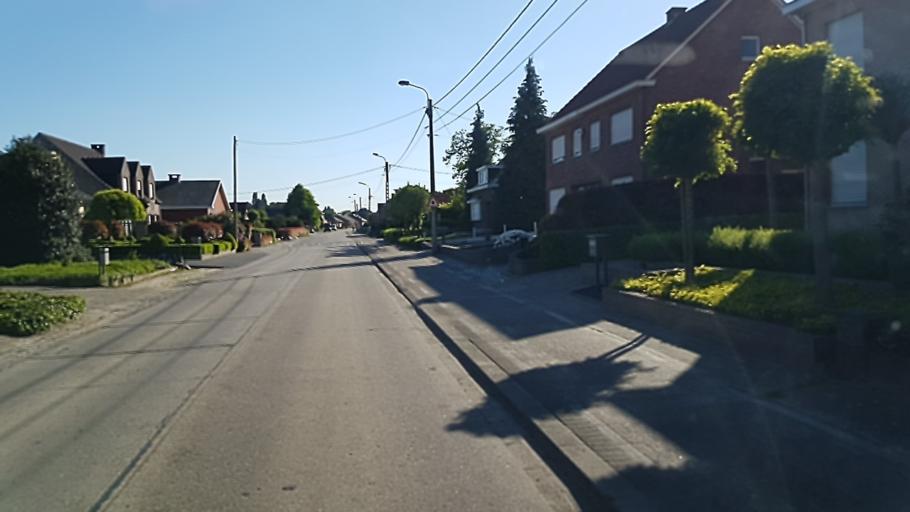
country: BE
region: Flanders
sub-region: Provincie Antwerpen
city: Berlaar
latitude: 51.0853
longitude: 4.6808
